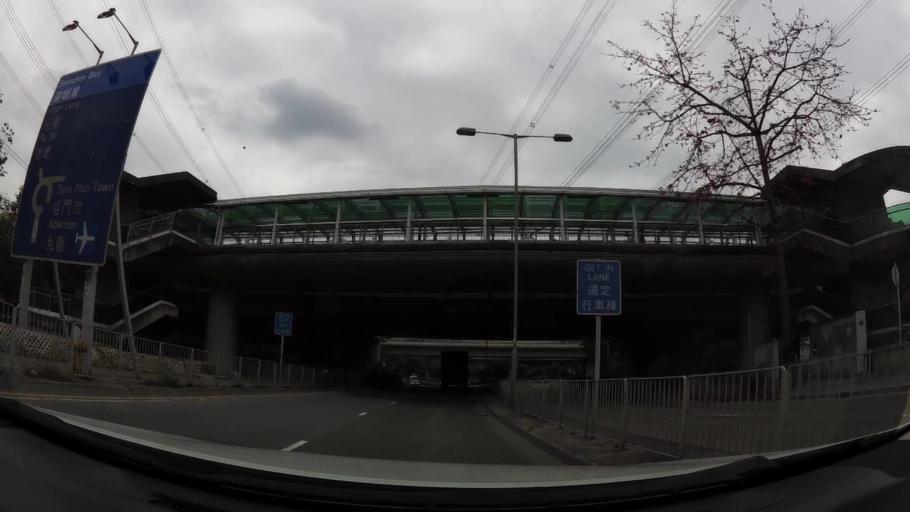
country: HK
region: Tuen Mun
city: Tuen Mun
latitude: 22.4155
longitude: 113.9800
